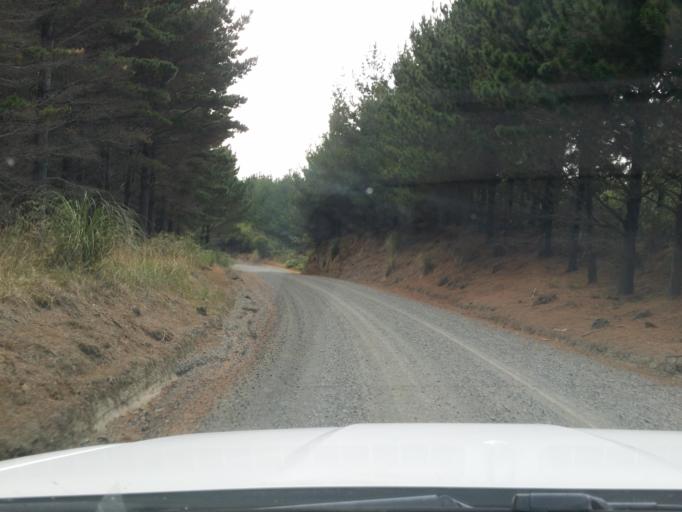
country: NZ
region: Northland
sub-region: Kaipara District
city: Dargaville
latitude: -36.2369
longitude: 174.0629
